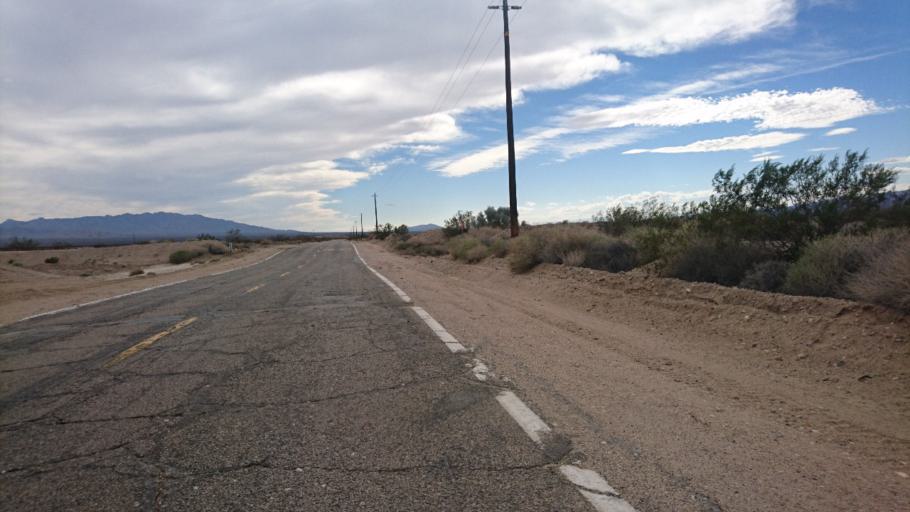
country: US
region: California
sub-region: San Bernardino County
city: Needles
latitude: 34.7645
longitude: -115.2153
